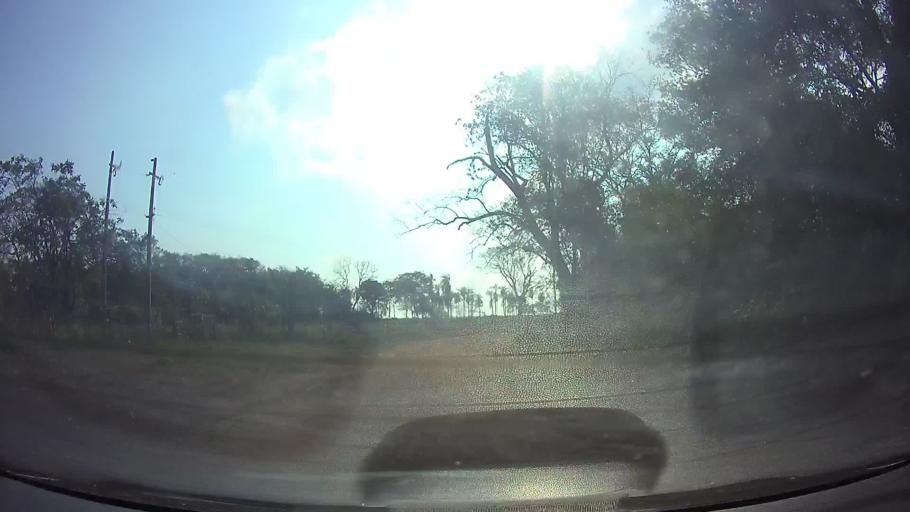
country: PY
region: Cordillera
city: Arroyos y Esteros
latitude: -25.0228
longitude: -57.1898
